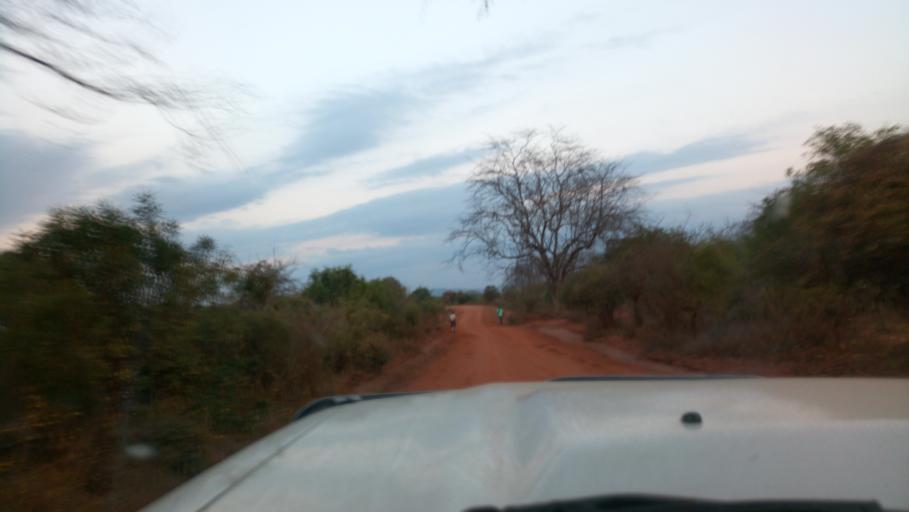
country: KE
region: Kitui
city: Kitui
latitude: -1.7295
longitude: 38.1995
